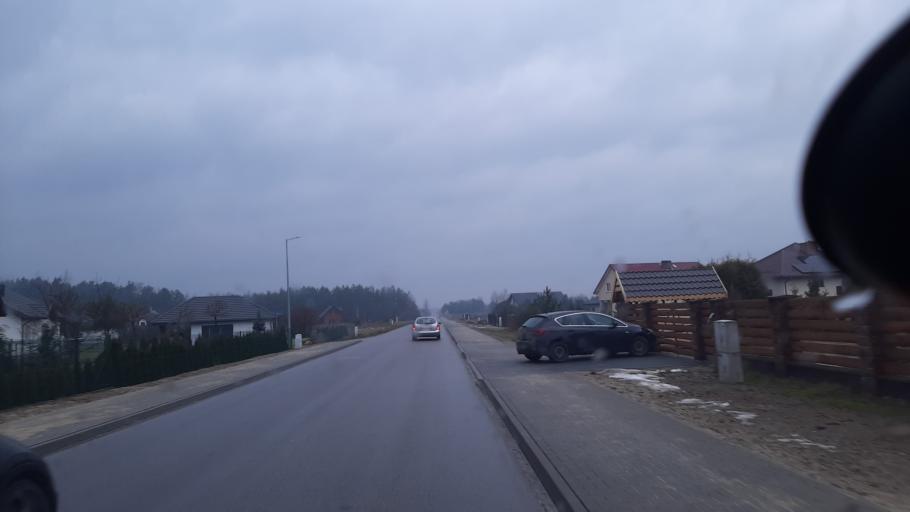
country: PL
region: Lublin Voivodeship
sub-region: Powiat lubartowski
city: Serniki
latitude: 51.4419
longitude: 22.6543
